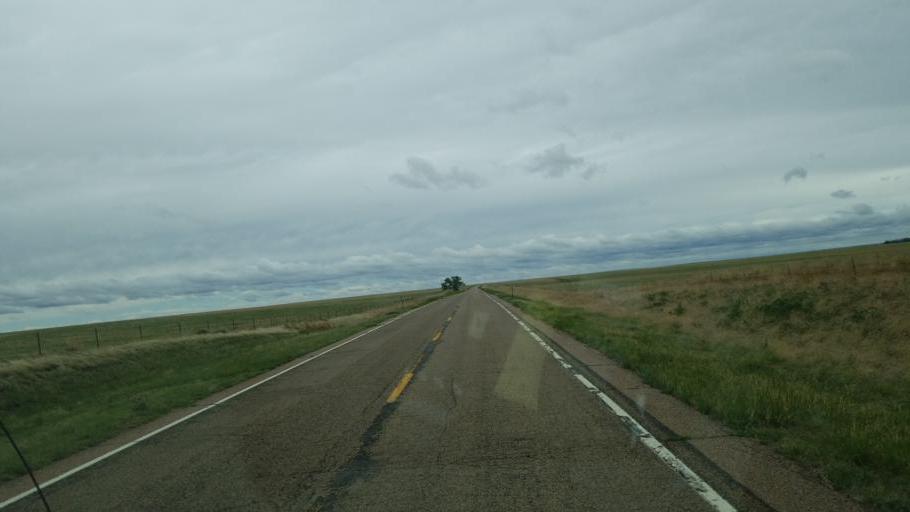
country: US
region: Colorado
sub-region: Lincoln County
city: Hugo
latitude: 38.8522
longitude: -103.7269
